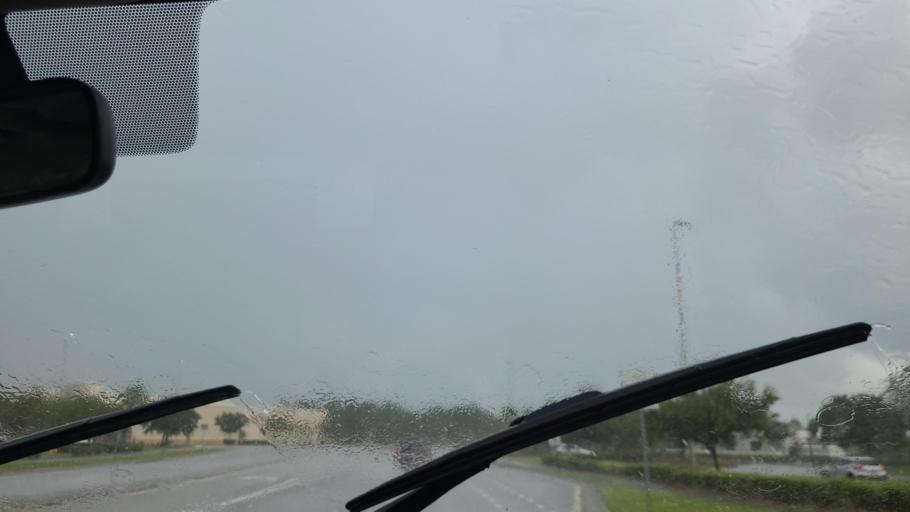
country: US
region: Florida
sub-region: Brevard County
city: West Melbourne
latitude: 28.0381
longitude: -80.6629
